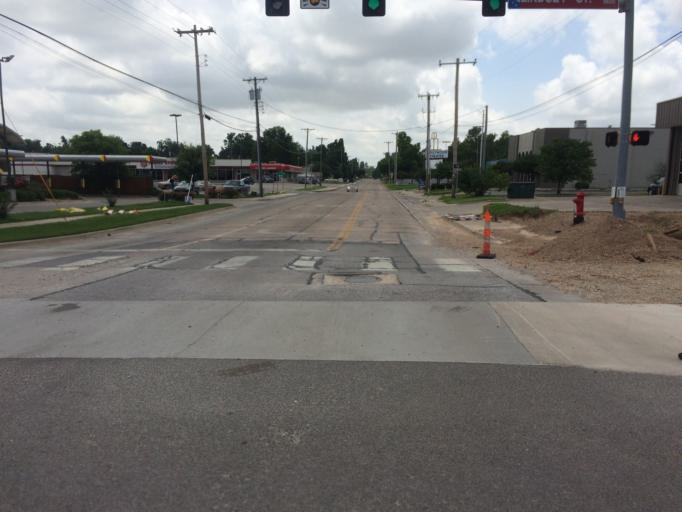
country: US
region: Oklahoma
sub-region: Cleveland County
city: Norman
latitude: 35.2040
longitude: -97.4678
